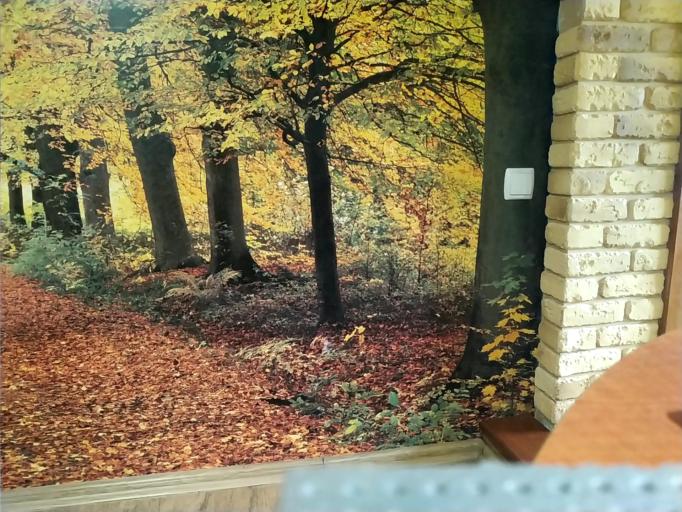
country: RU
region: Tverskaya
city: Kalashnikovo
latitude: 57.2755
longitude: 35.2494
